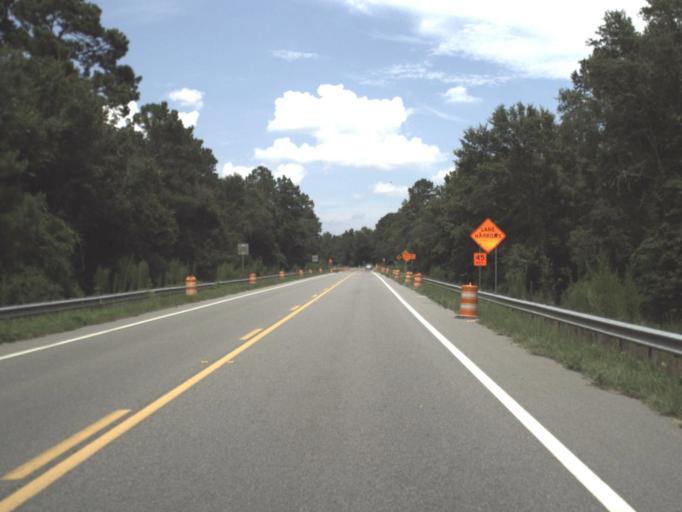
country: US
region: Florida
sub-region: Madison County
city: Madison
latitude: 30.6301
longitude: -83.3152
